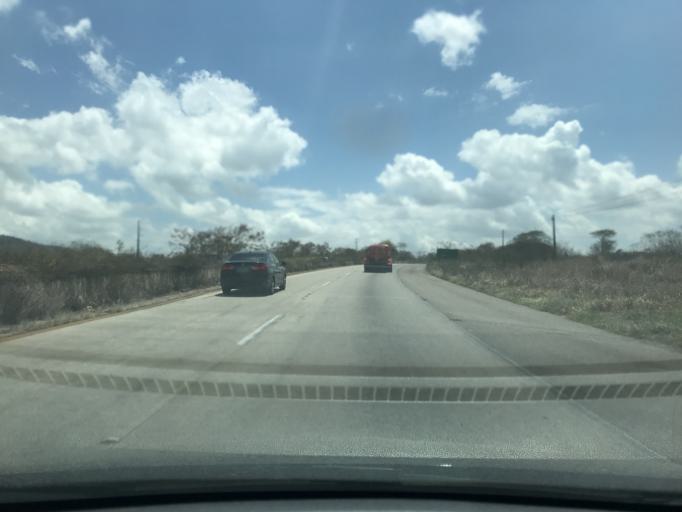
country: BR
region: Pernambuco
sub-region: Bezerros
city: Bezerros
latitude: -8.2962
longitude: -35.8286
